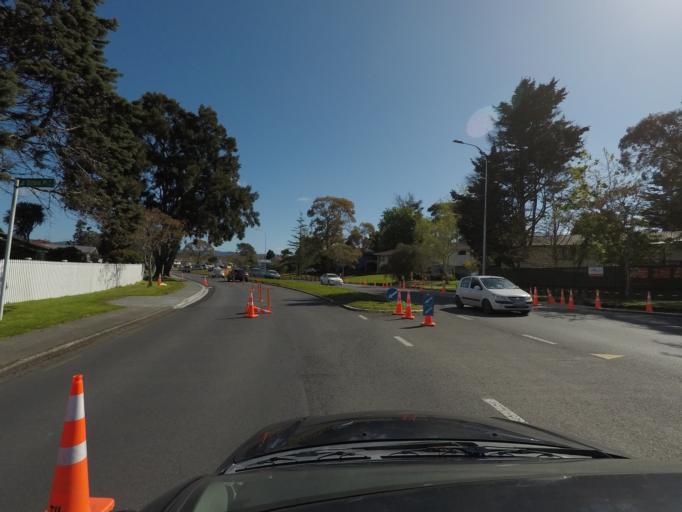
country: NZ
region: Auckland
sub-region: Auckland
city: Rosebank
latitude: -36.8563
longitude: 174.6204
